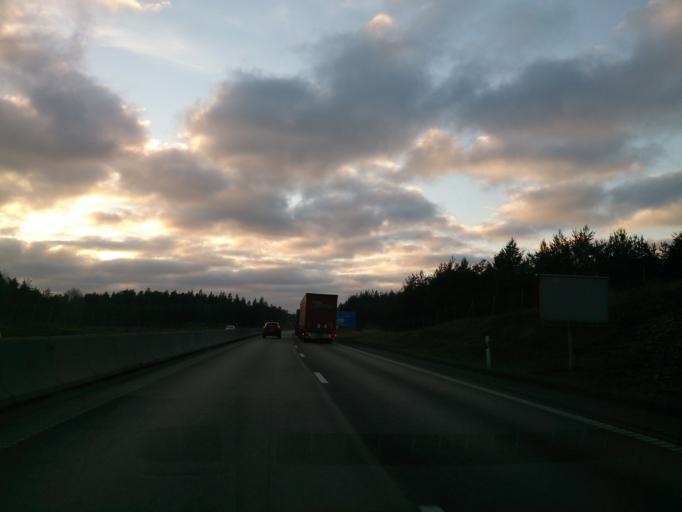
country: SE
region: OEstergoetland
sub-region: Norrkopings Kommun
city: Kimstad
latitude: 58.4934
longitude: 15.9674
